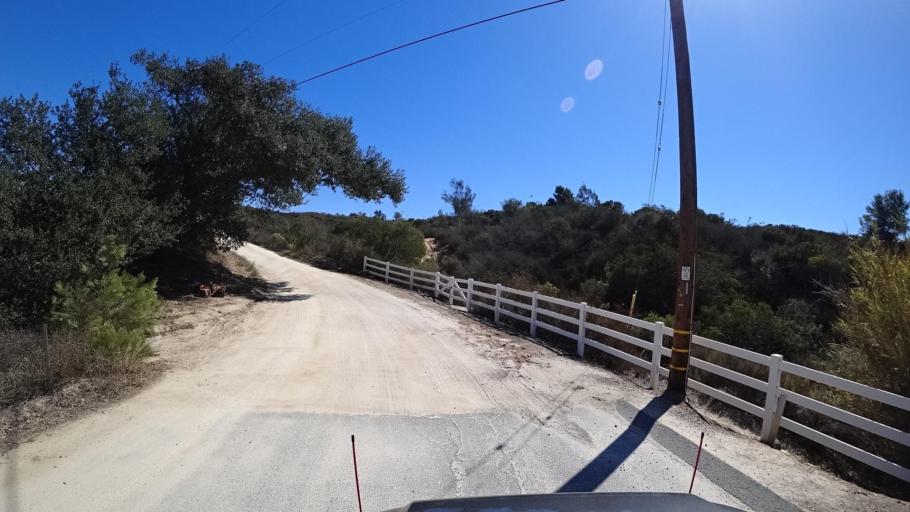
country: US
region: California
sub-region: San Diego County
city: Harbison Canyon
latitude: 32.7878
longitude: -116.8077
